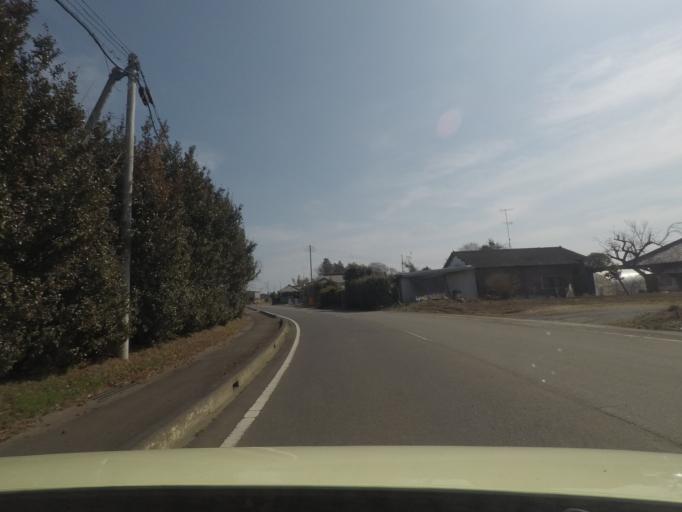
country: JP
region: Ibaraki
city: Ishioka
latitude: 36.1966
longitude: 140.3264
